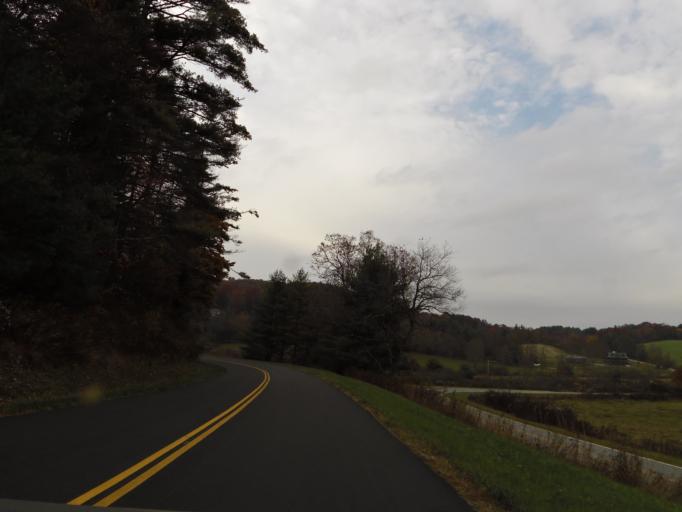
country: US
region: North Carolina
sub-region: Alleghany County
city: Sparta
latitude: 36.4012
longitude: -81.2156
